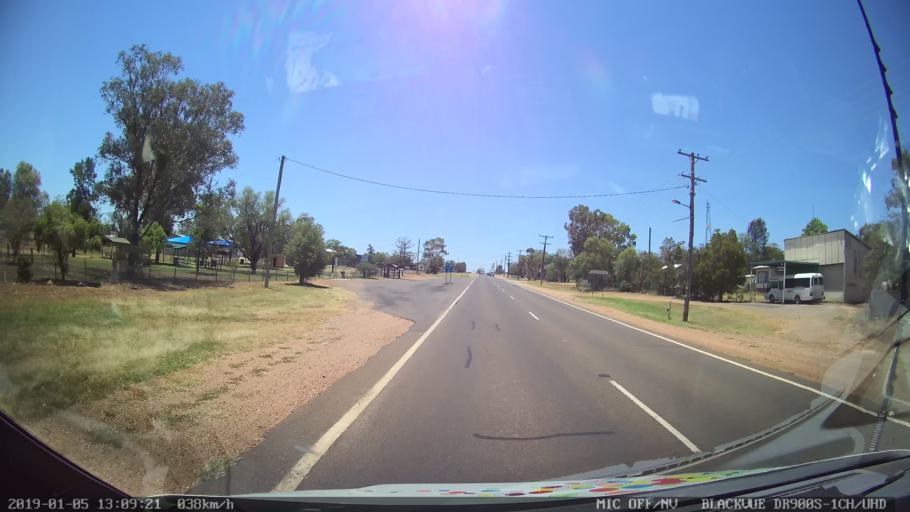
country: AU
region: New South Wales
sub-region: Gunnedah
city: Gunnedah
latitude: -31.0982
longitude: 149.9095
